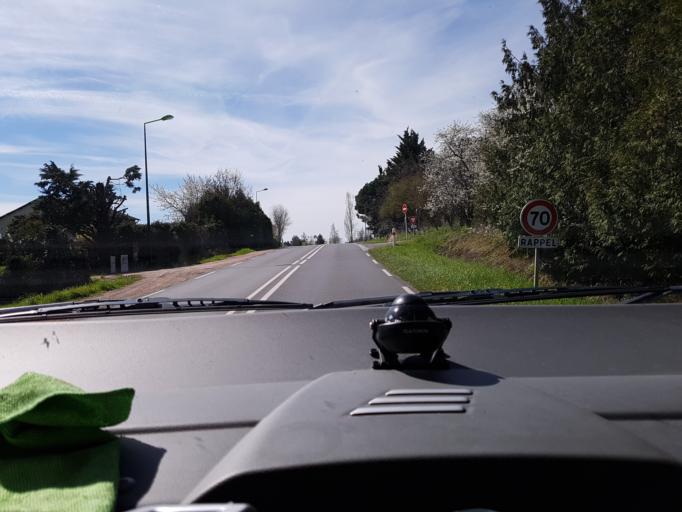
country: FR
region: Auvergne
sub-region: Departement de l'Allier
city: Creuzier-le-Vieux
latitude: 46.1587
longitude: 3.4612
